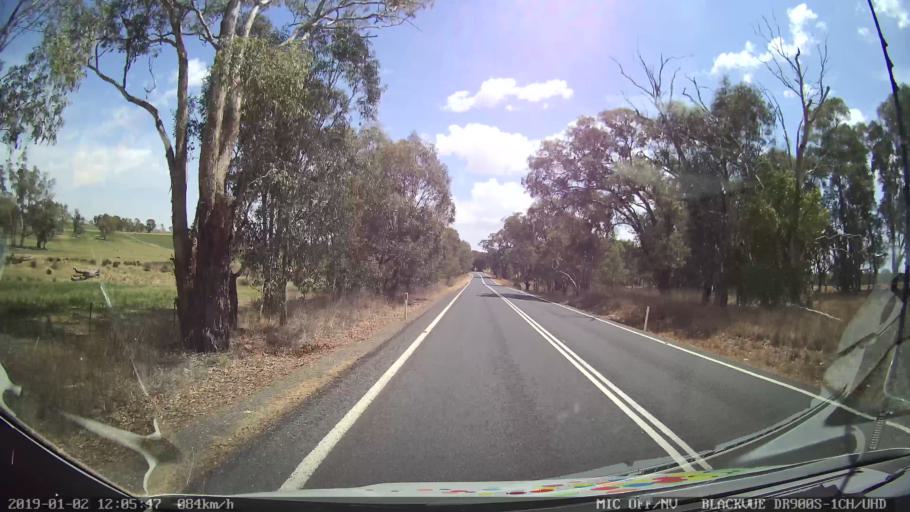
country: AU
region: New South Wales
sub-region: Young
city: Young
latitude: -34.5103
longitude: 148.2995
